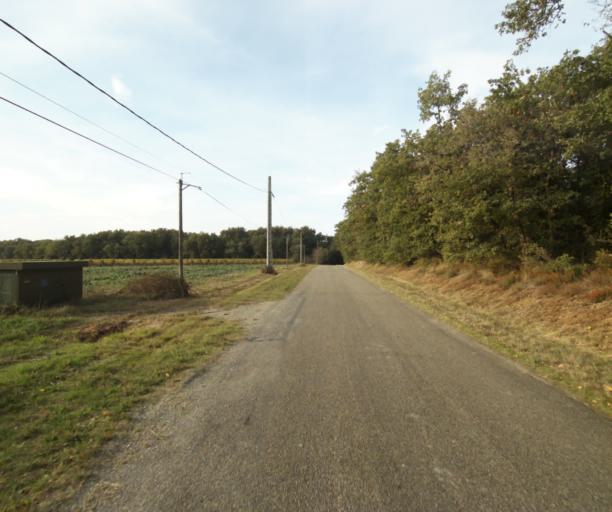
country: FR
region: Midi-Pyrenees
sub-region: Departement du Tarn-et-Garonne
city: Campsas
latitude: 43.8769
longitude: 1.3246
